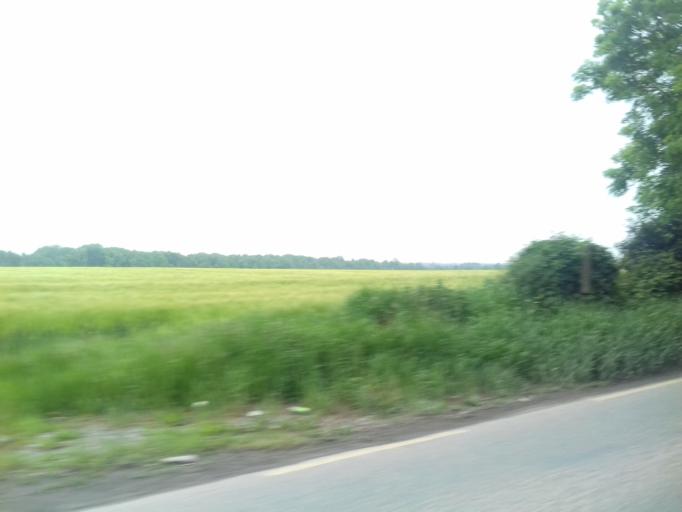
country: IE
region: Leinster
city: Donabate
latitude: 53.4807
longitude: -6.1716
